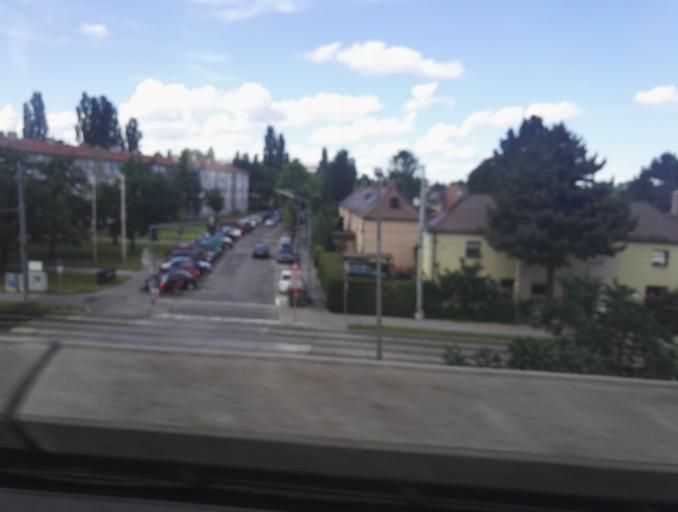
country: AT
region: Lower Austria
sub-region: Politischer Bezirk Wien-Umgebung
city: Gerasdorf bei Wien
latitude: 48.2201
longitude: 16.4620
